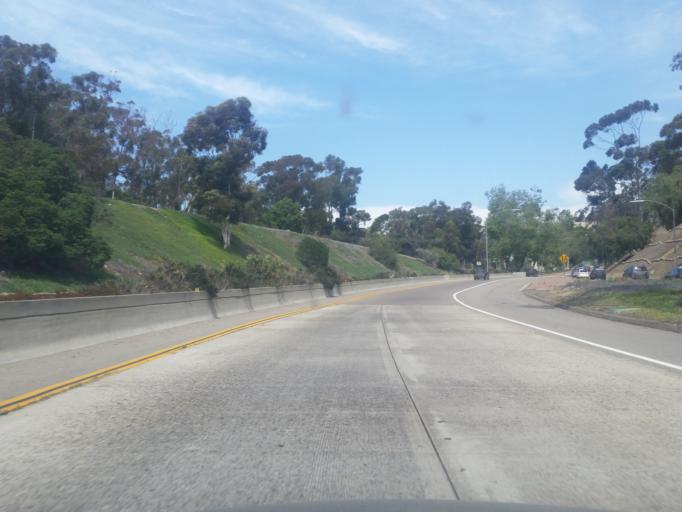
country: US
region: California
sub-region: San Diego County
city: San Diego
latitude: 32.7269
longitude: -117.1559
